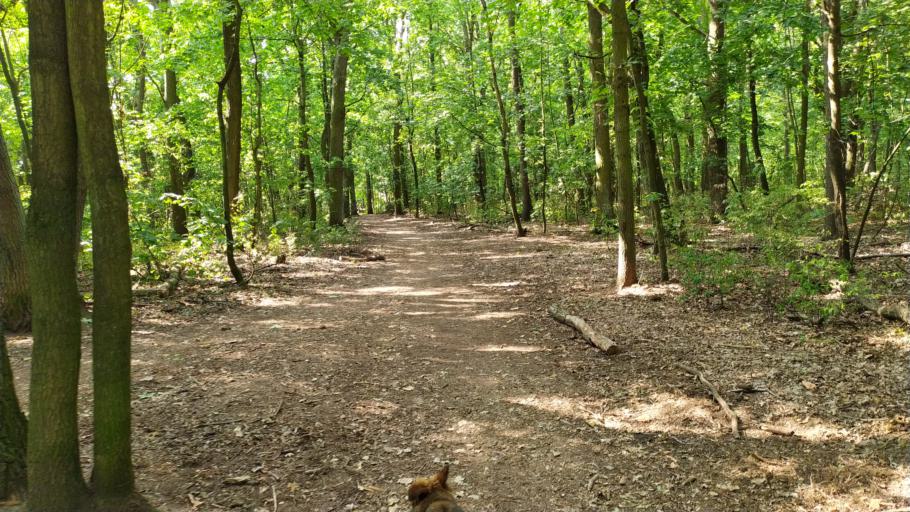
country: DE
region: Berlin
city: Grunau
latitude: 52.4169
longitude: 13.5964
